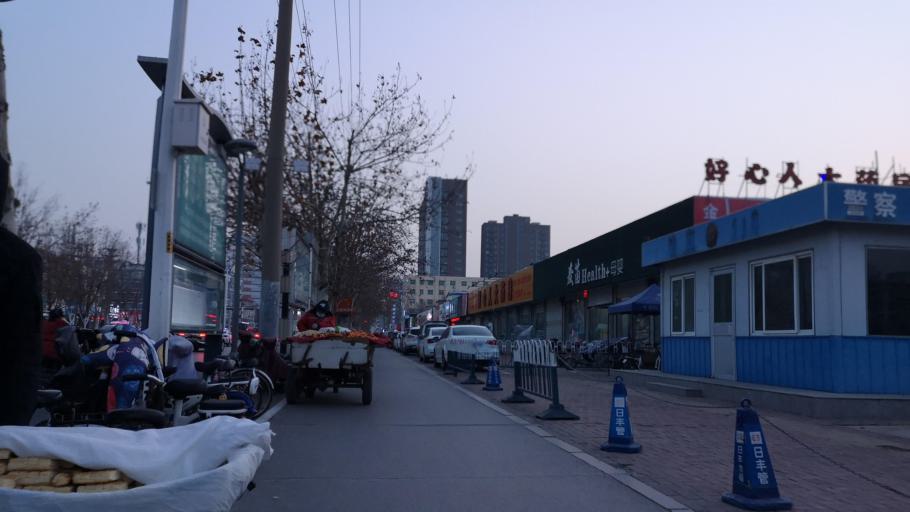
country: CN
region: Henan Sheng
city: Zhongyuanlu
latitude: 35.7706
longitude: 115.0692
